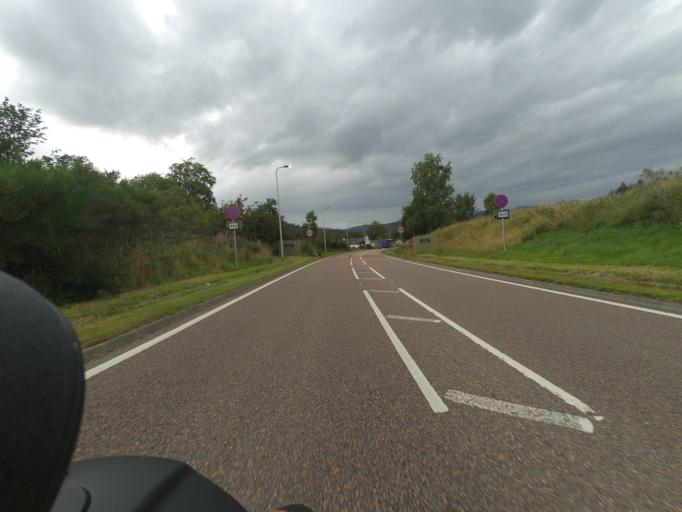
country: GB
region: Scotland
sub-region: Highland
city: Muir of Ord
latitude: 57.5630
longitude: -4.5742
